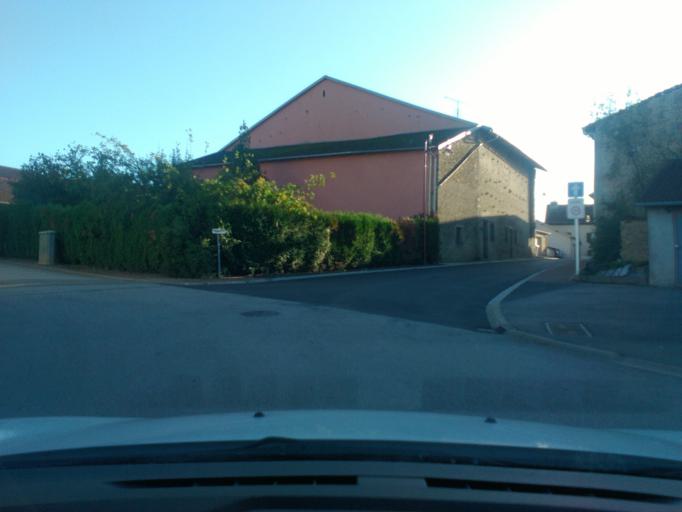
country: FR
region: Lorraine
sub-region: Departement des Vosges
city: Rambervillers
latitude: 48.2945
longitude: 6.6038
